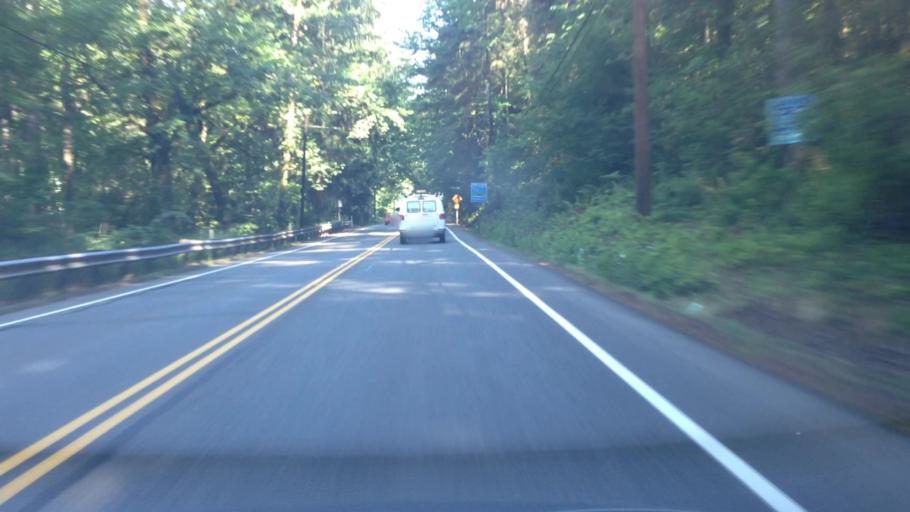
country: US
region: Washington
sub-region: King County
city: Duvall
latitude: 47.7549
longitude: -122.0217
